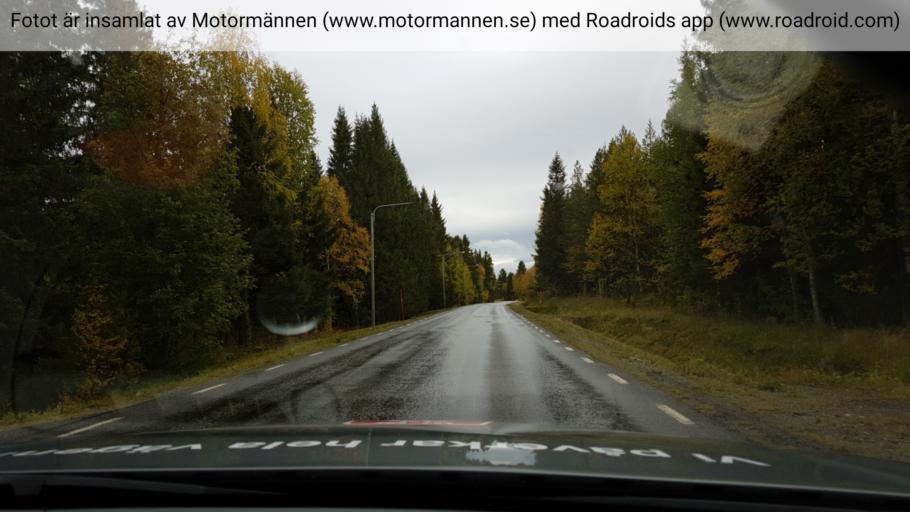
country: SE
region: Vaesterbotten
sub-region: Vilhelmina Kommun
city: Sjoberg
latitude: 64.6700
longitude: 16.2981
